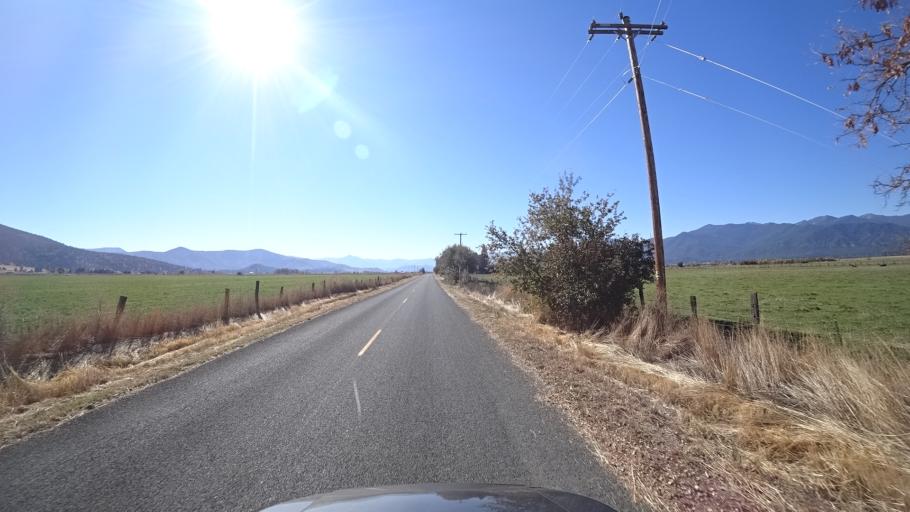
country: US
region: California
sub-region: Siskiyou County
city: Yreka
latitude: 41.5341
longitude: -122.8578
